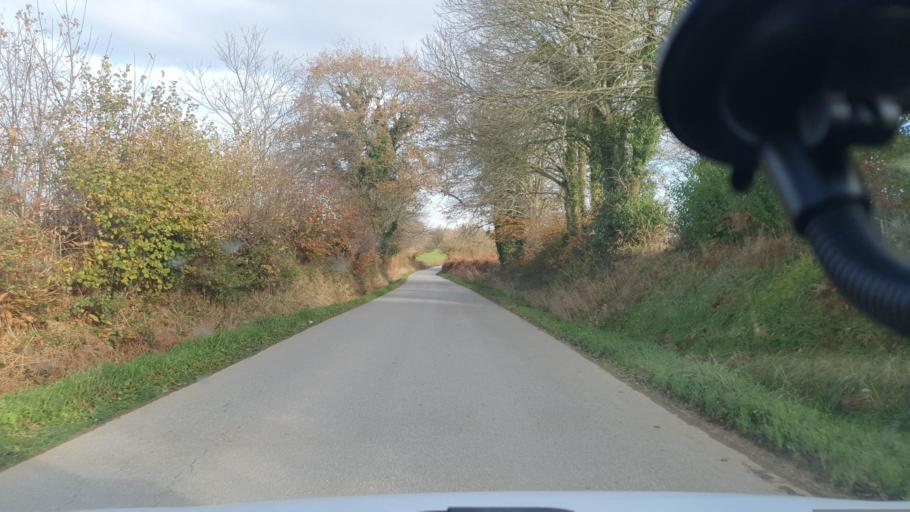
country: FR
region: Brittany
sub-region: Departement du Finistere
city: Briec
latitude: 48.0707
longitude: -4.0133
